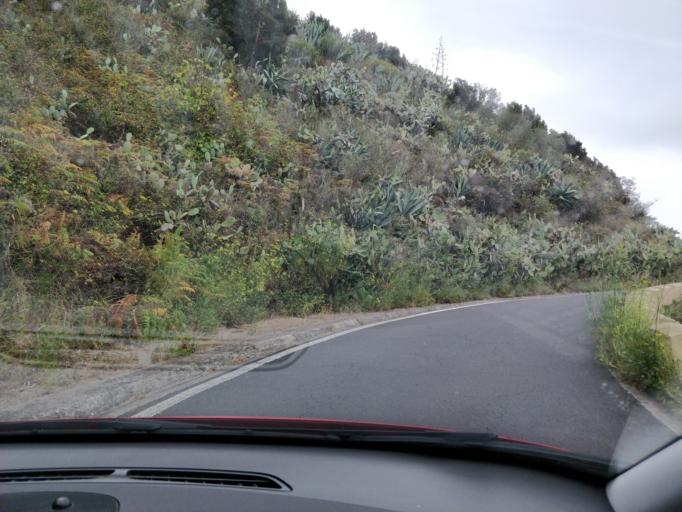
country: ES
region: Canary Islands
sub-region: Provincia de Santa Cruz de Tenerife
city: Santiago del Teide
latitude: 28.3224
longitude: -16.8496
